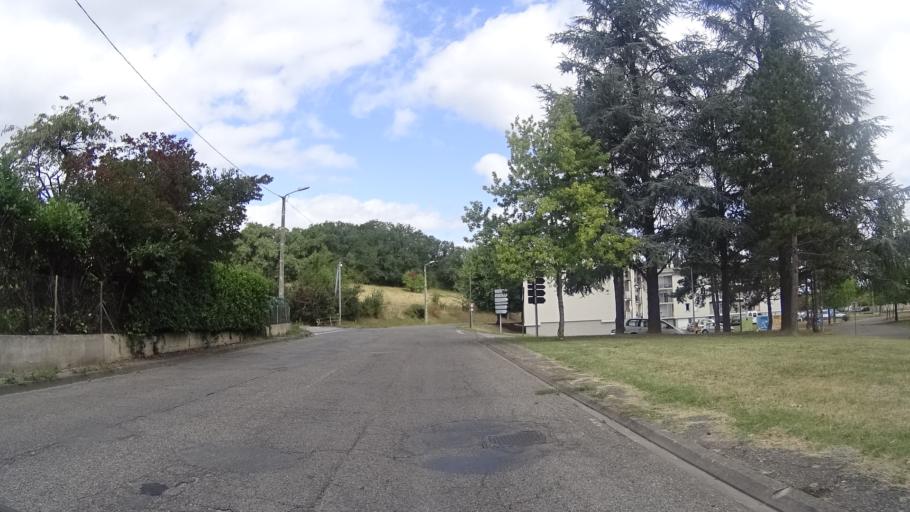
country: FR
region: Aquitaine
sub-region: Departement du Lot-et-Garonne
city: Agen
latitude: 44.2143
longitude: 0.6460
